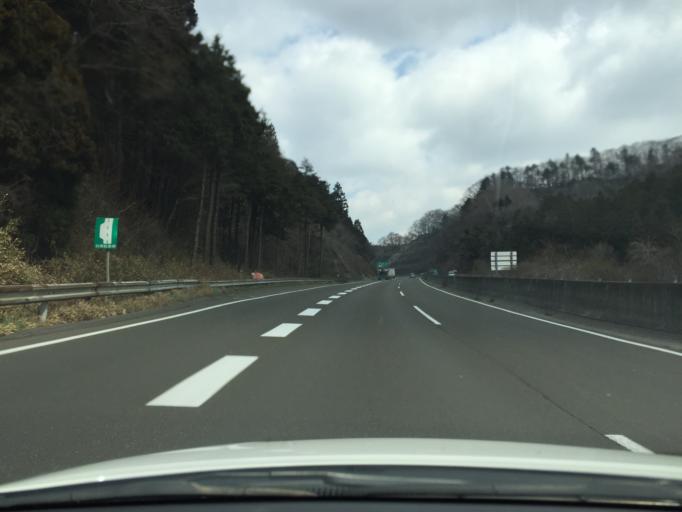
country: JP
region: Miyagi
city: Sendai
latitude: 38.2446
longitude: 140.8172
